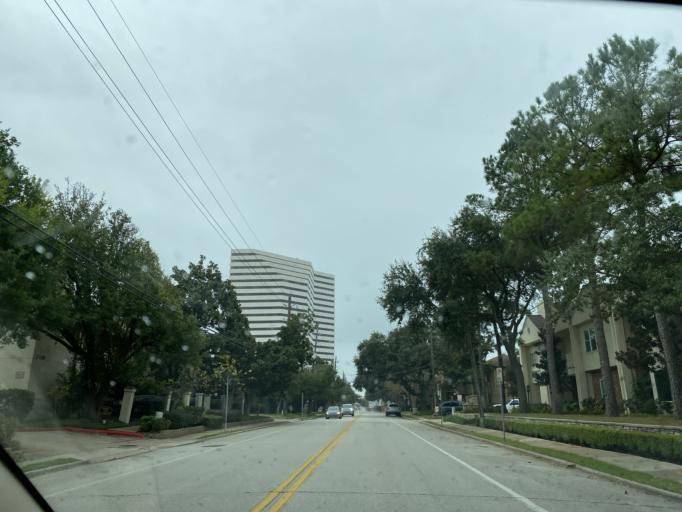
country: US
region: Texas
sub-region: Harris County
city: Hunters Creek Village
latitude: 29.7415
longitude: -95.4795
